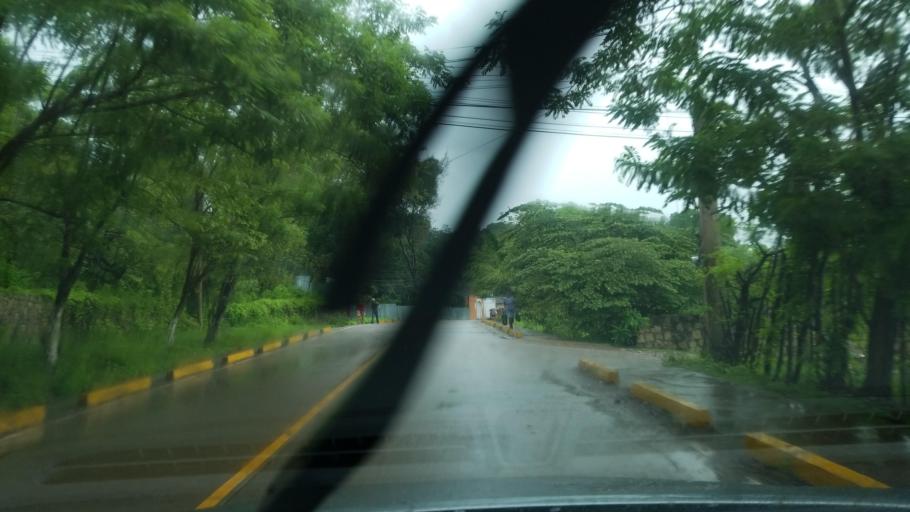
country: HN
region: Copan
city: Copan
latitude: 14.8389
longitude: -89.1613
